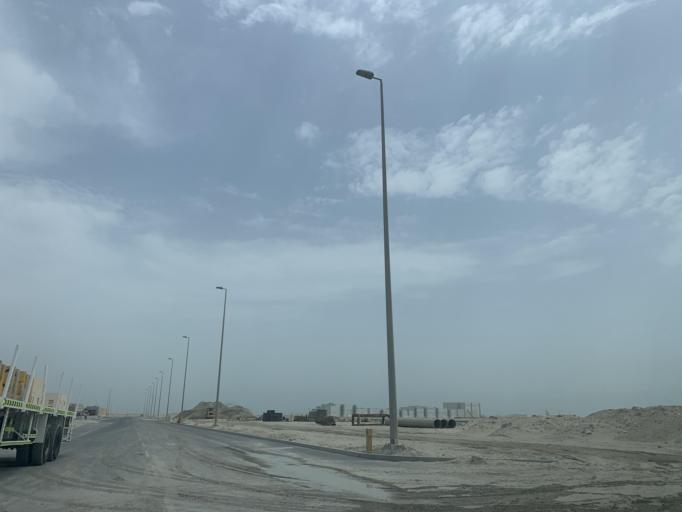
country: BH
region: Muharraq
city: Al Hadd
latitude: 26.2202
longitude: 50.6890
